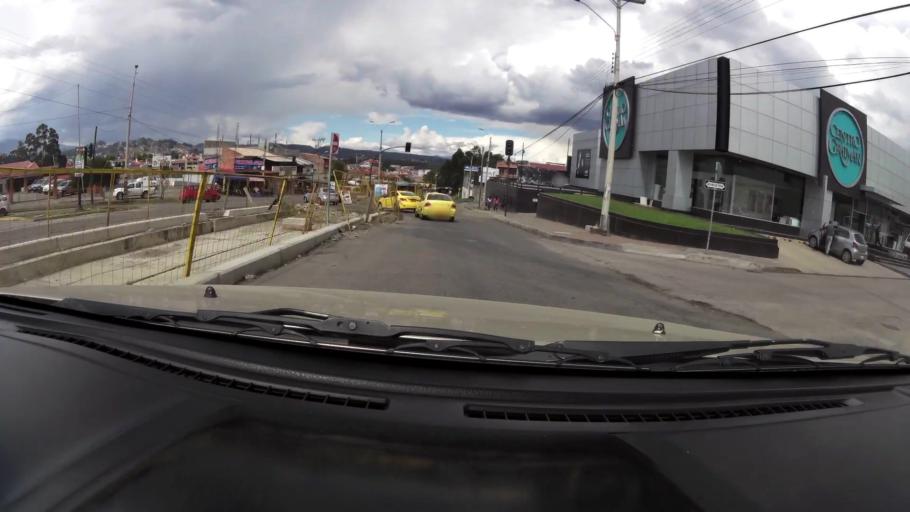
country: EC
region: Azuay
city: Cuenca
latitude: -2.8843
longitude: -78.9813
